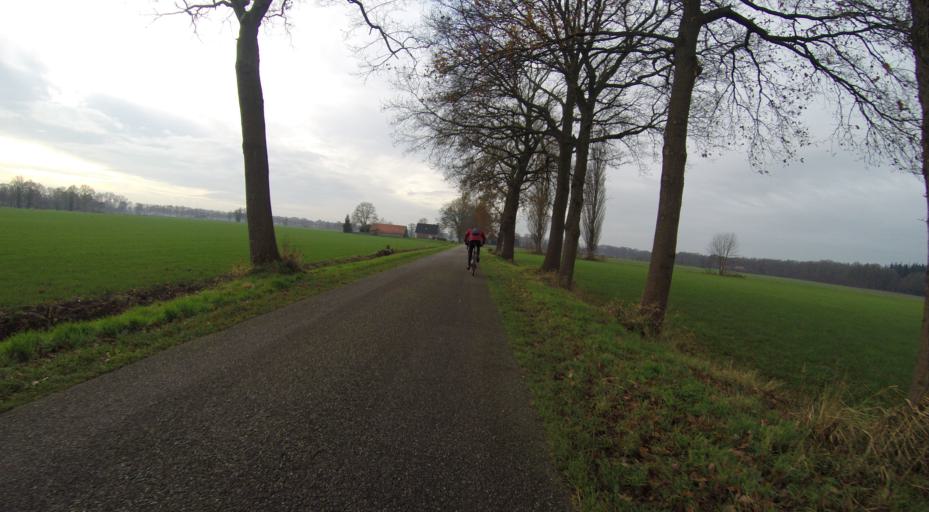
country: NL
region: Gelderland
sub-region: Gemeente Lochem
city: Lochem
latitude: 52.1453
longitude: 6.4024
